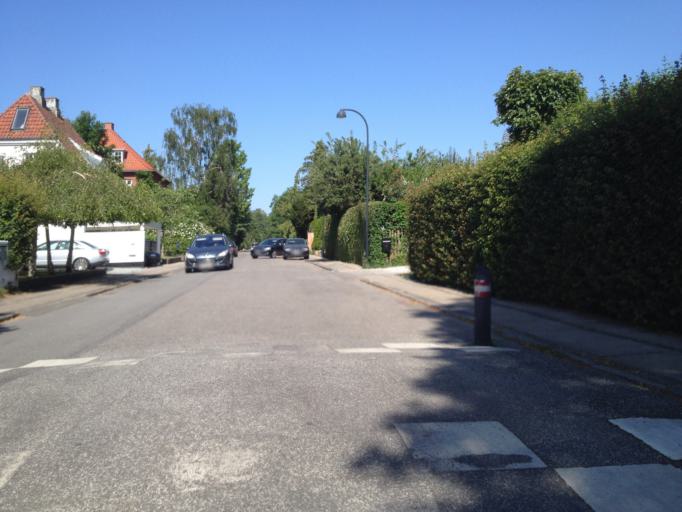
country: DK
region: Capital Region
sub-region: Gentofte Kommune
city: Charlottenlund
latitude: 55.7465
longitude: 12.5765
